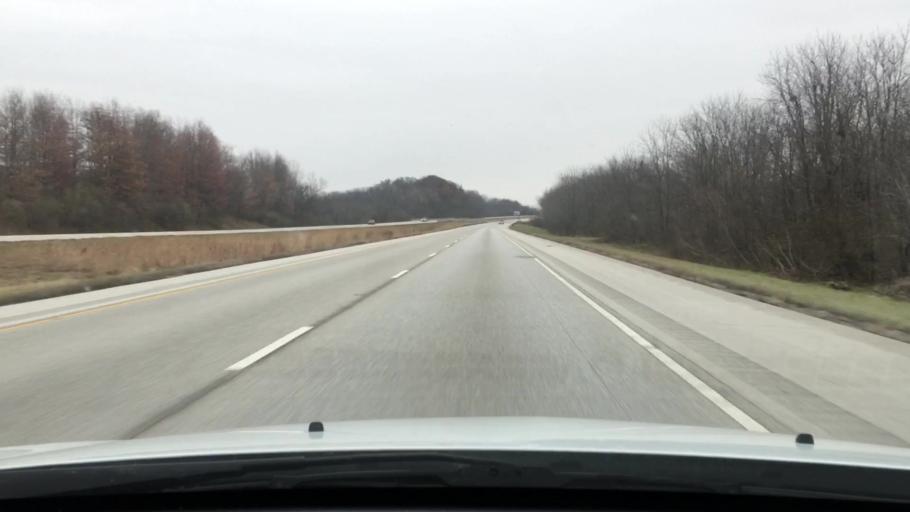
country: US
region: Illinois
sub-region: Scott County
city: Winchester
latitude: 39.6812
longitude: -90.3994
